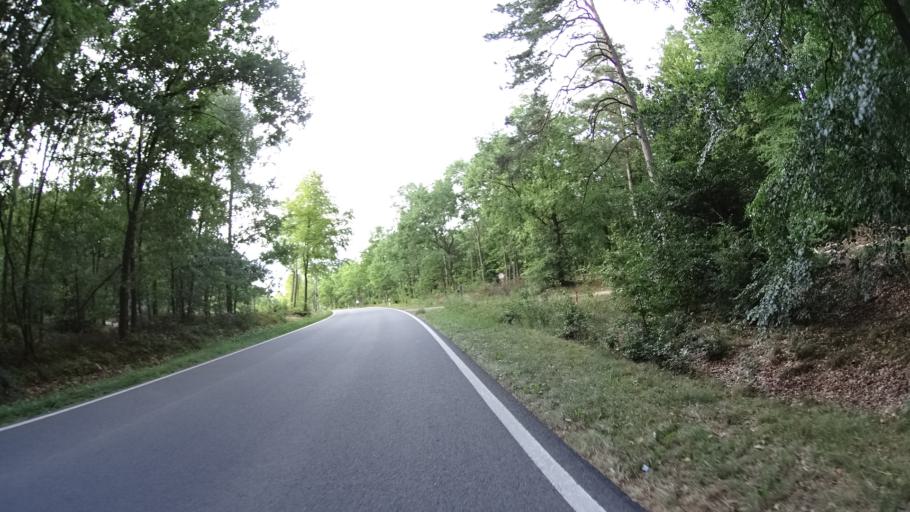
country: DE
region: Lower Saxony
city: Undeloh
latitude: 53.1692
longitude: 9.8942
